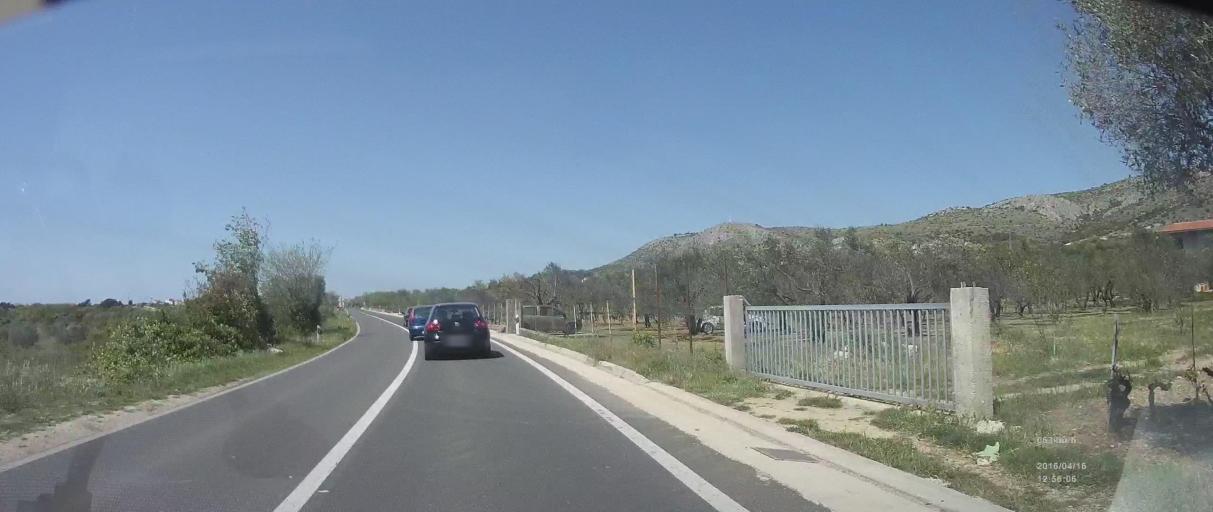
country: HR
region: Sibensko-Kniniska
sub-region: Grad Sibenik
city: Brodarica
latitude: 43.6990
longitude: 15.9452
